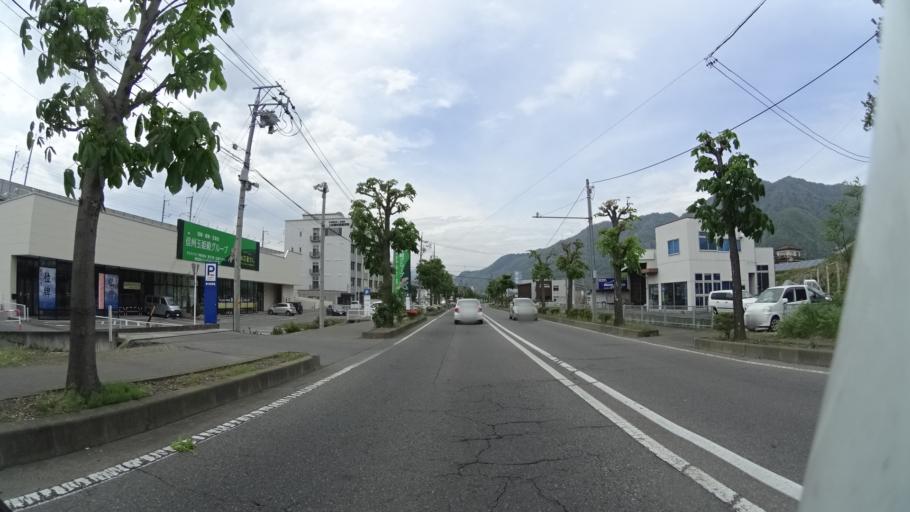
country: JP
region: Nagano
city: Ueda
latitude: 36.4075
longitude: 138.2339
